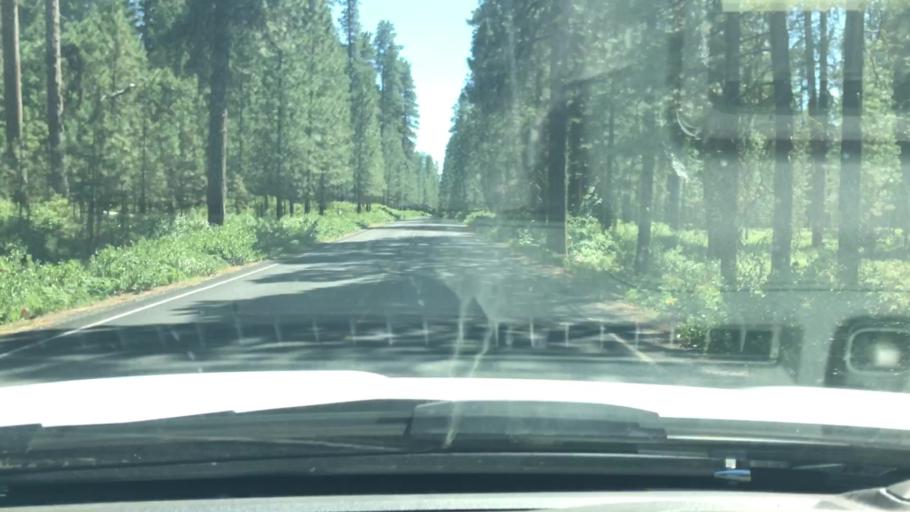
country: US
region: Oregon
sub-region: Deschutes County
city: Sisters
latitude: 44.4177
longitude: -121.6700
